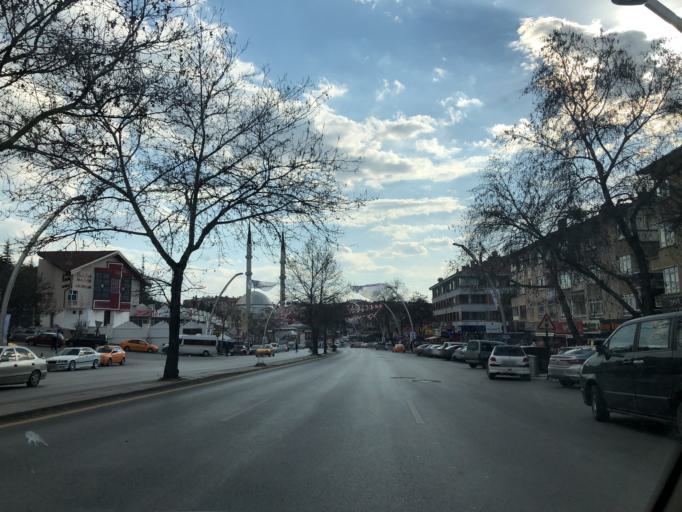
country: TR
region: Ankara
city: Mamak
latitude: 39.9863
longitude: 32.8645
